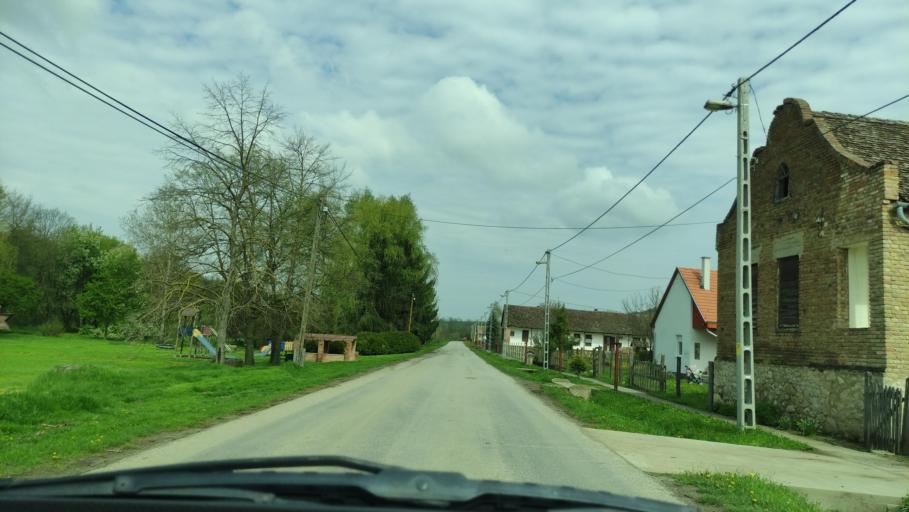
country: HU
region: Baranya
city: Magocs
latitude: 46.2775
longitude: 18.2084
